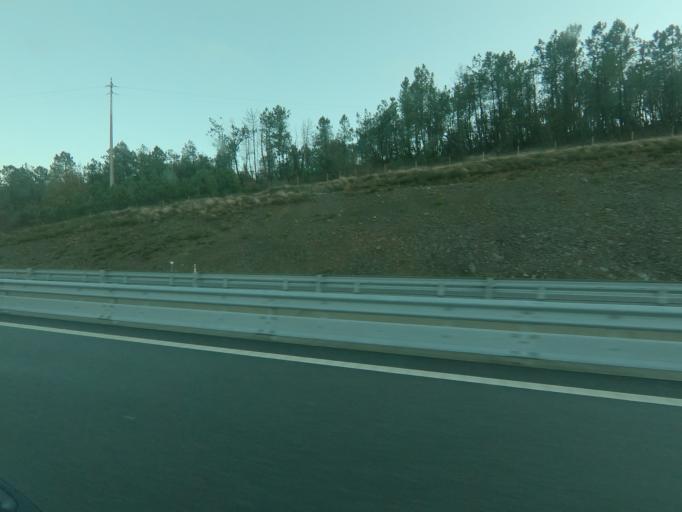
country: PT
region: Vila Real
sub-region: Santa Marta de Penaguiao
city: Santa Marta de Penaguiao
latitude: 41.2791
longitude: -7.8503
